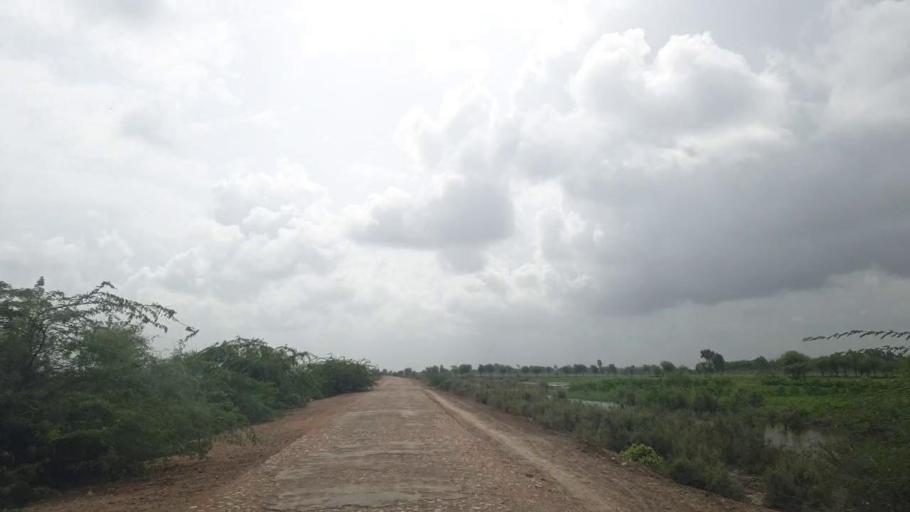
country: PK
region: Sindh
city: Tando Bago
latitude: 24.8270
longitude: 69.0829
